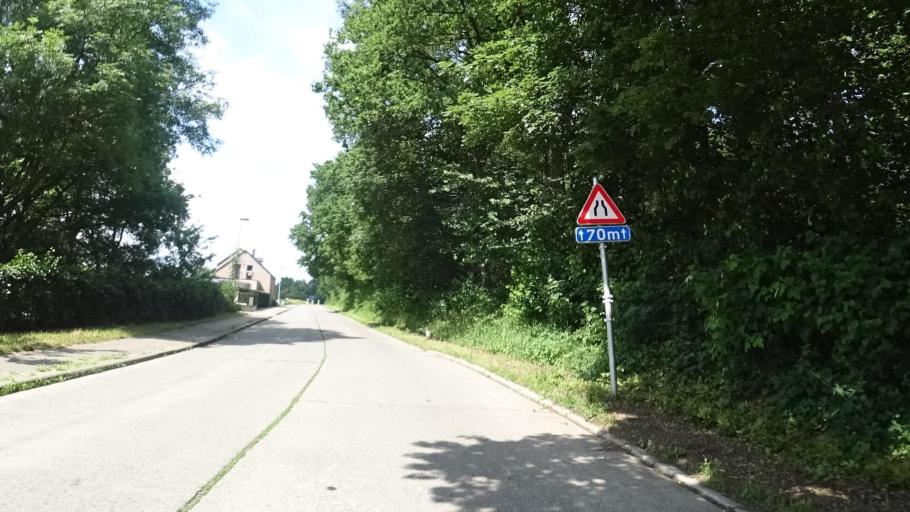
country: BE
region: Wallonia
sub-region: Province du Brabant Wallon
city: Perwez
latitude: 50.5927
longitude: 4.7799
